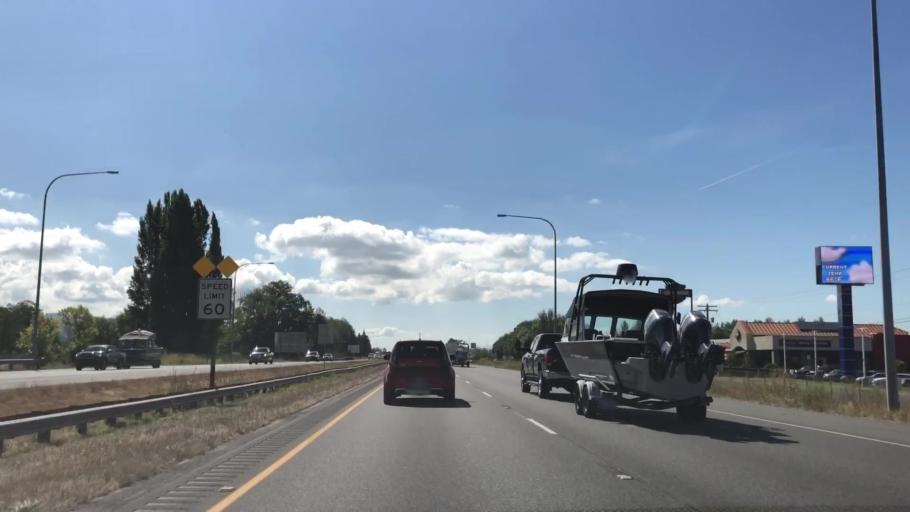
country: US
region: Washington
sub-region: Skagit County
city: Burlington
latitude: 48.4614
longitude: -122.3416
